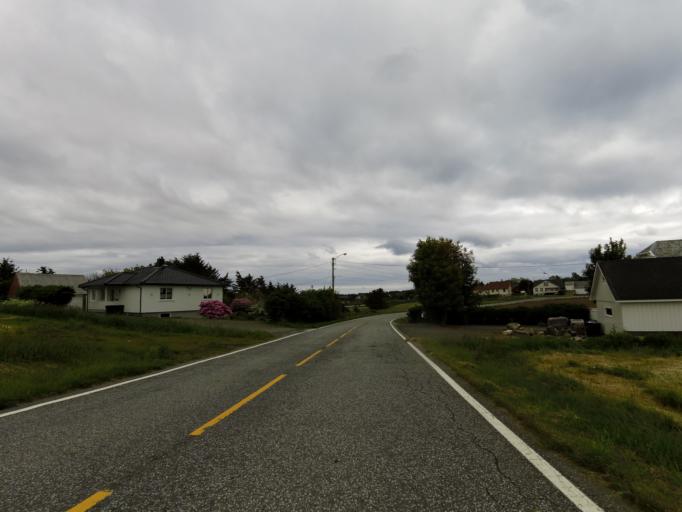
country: NO
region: Vest-Agder
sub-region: Farsund
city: Vestbygd
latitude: 58.1225
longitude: 6.6035
